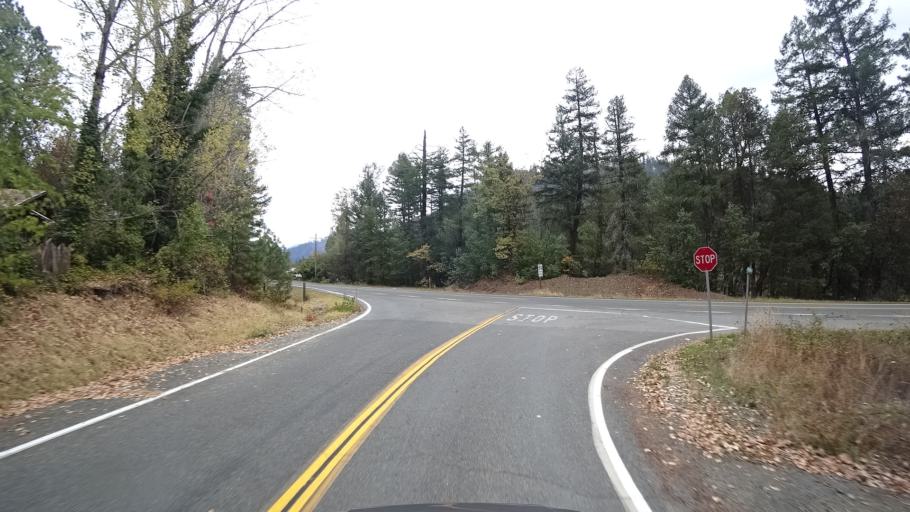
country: US
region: California
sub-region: Siskiyou County
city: Happy Camp
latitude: 41.7872
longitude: -123.3927
